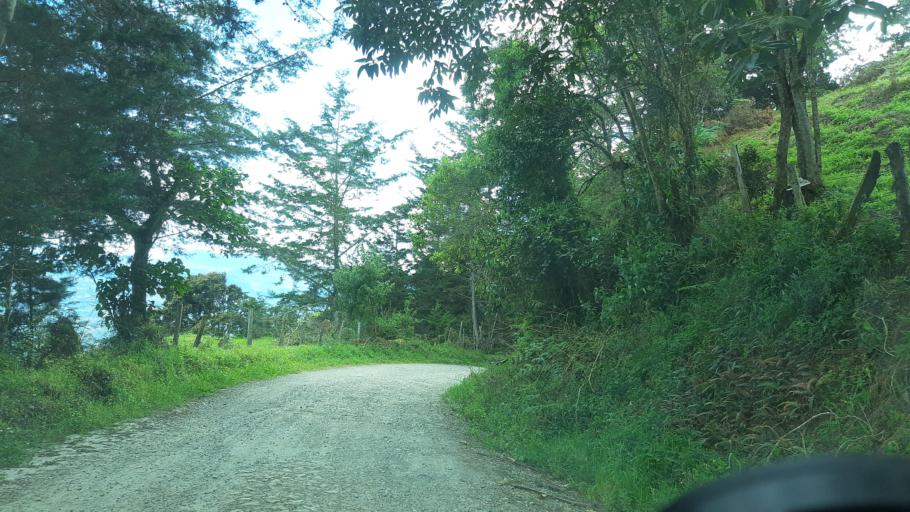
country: CO
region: Boyaca
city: Garagoa
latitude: 5.0500
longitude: -73.3537
